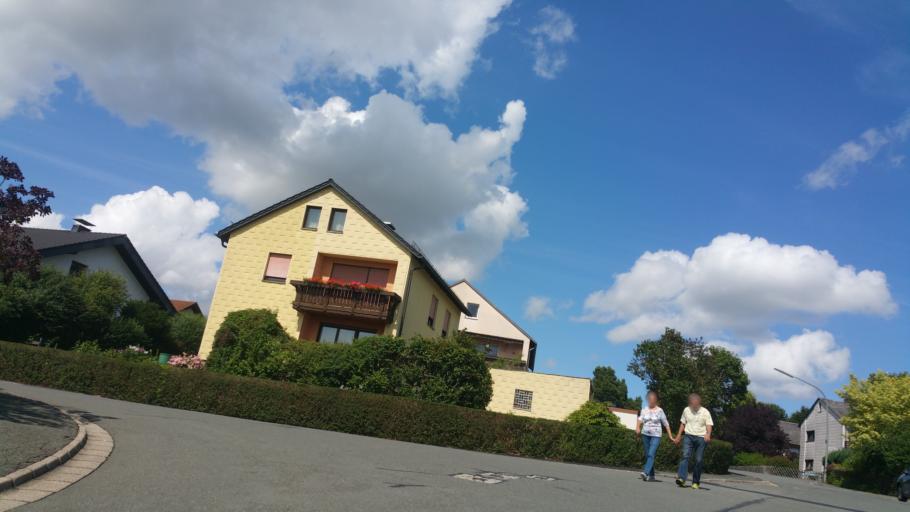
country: DE
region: Bavaria
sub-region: Upper Franconia
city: Oberkotzau
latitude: 50.2589
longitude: 11.9390
